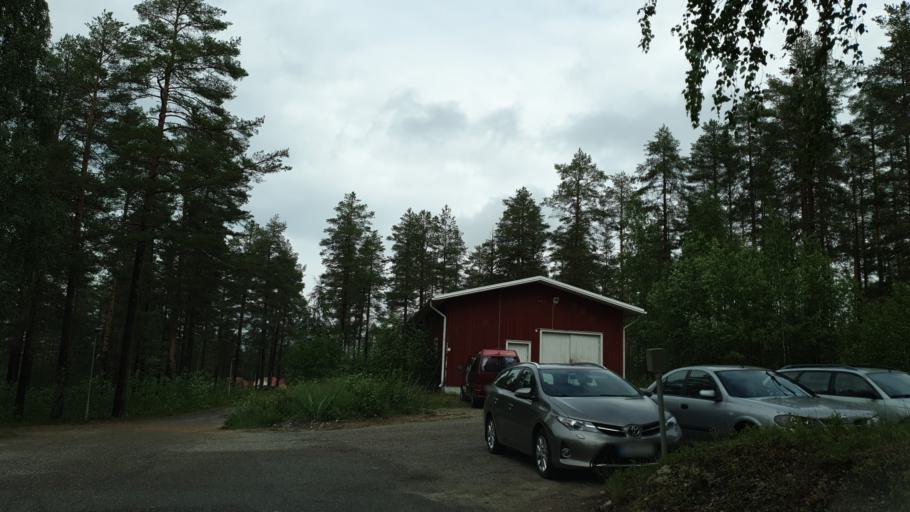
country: FI
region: Kainuu
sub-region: Kehys-Kainuu
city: Kuhmo
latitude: 64.0947
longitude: 29.4348
